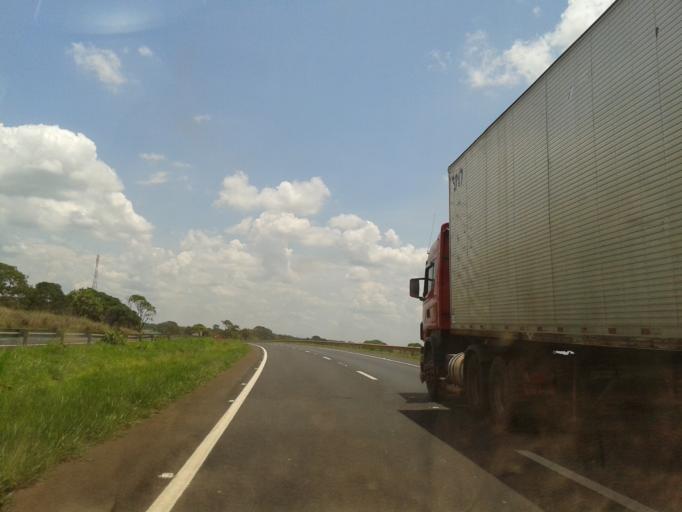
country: BR
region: Minas Gerais
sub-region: Monte Alegre De Minas
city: Monte Alegre de Minas
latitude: -18.8528
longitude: -48.7813
